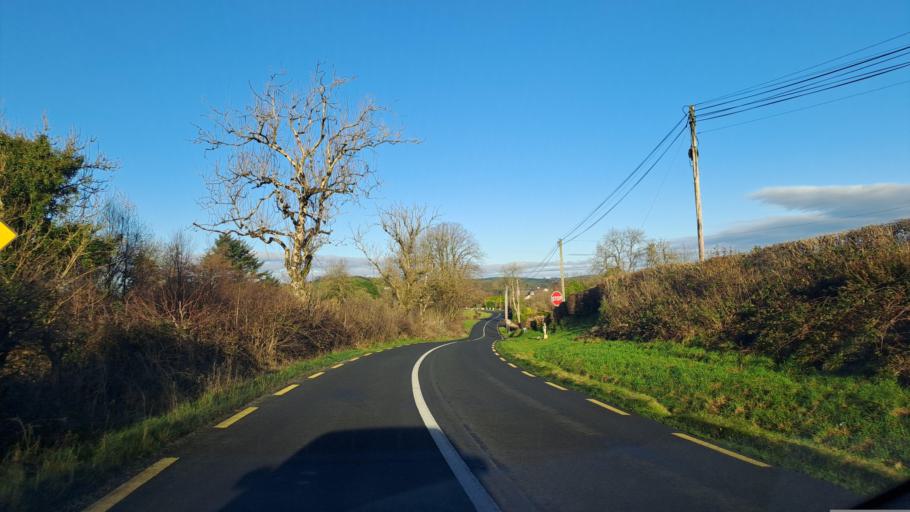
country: IE
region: Ulster
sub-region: An Cabhan
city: Bailieborough
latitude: 53.8855
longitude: -6.9644
